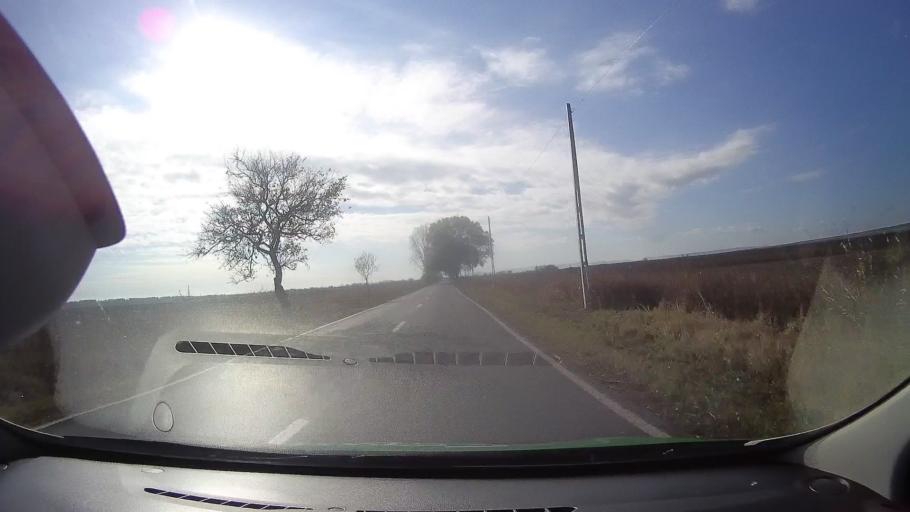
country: RO
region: Tulcea
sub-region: Comuna Valea Nucarilor
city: Agighiol
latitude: 44.9918
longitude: 28.8857
